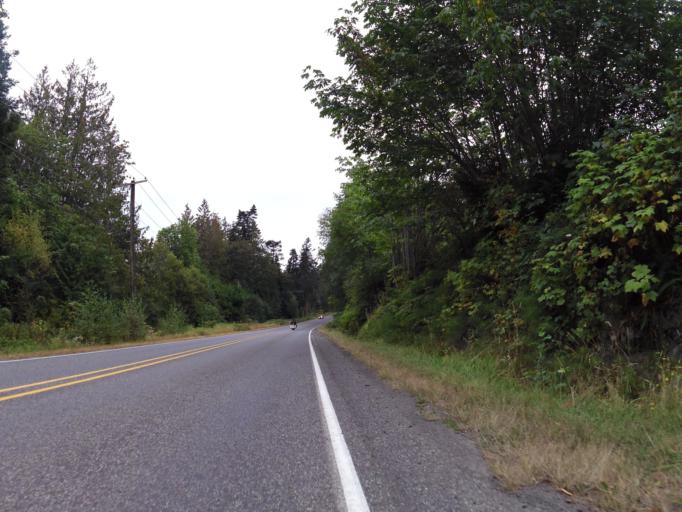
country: US
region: Washington
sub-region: Jefferson County
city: Port Ludlow
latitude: 47.9815
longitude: -122.7144
